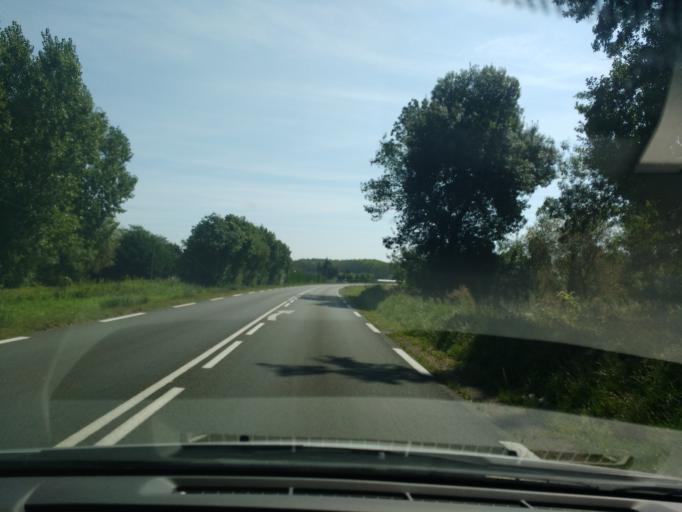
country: FR
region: Pays de la Loire
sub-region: Departement de Maine-et-Loire
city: Baune
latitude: 47.4733
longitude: -0.3145
